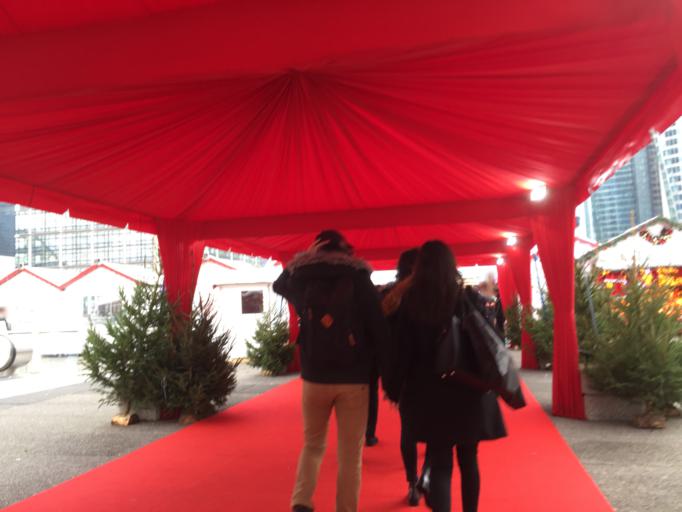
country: FR
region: Ile-de-France
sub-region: Departement des Hauts-de-Seine
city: La Defense
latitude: 48.8916
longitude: 2.2392
